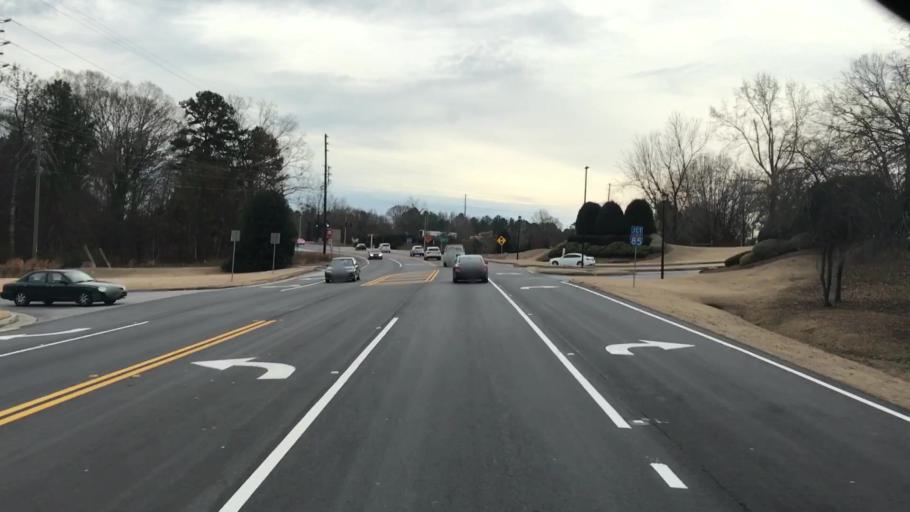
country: US
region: Georgia
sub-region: Jackson County
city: Braselton
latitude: 34.1007
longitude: -83.8140
